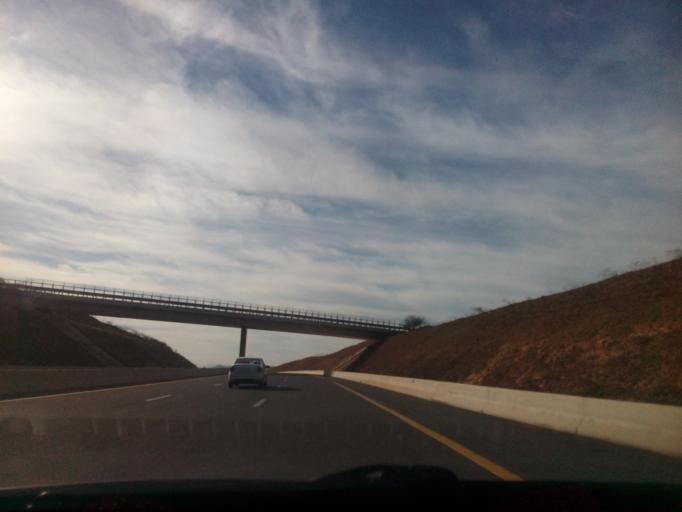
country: DZ
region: Tlemcen
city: Beni Mester
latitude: 34.9009
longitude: -1.5875
